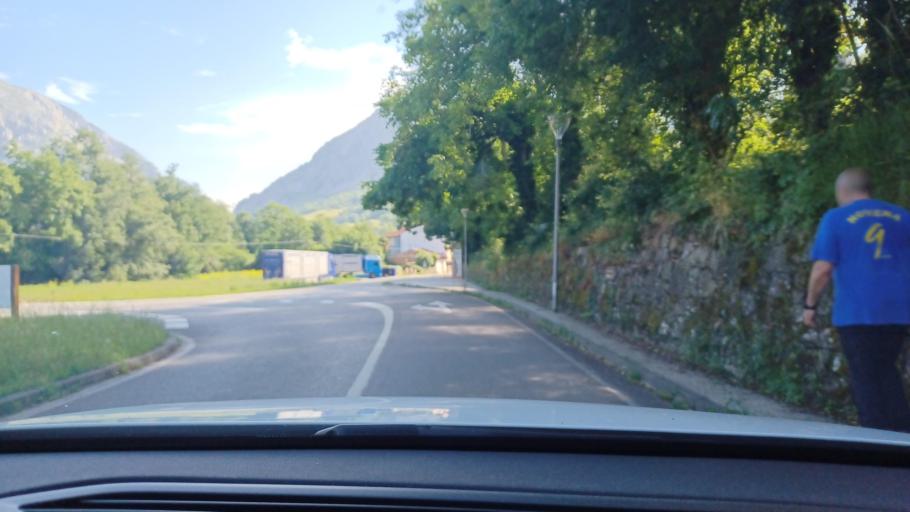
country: ES
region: Asturias
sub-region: Province of Asturias
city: La Plaza
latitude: 43.1596
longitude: -6.1004
